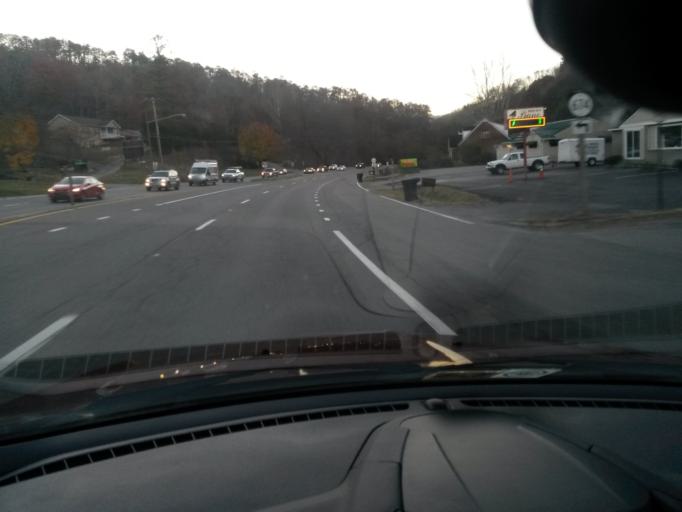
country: US
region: Virginia
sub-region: Roanoke County
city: Narrows
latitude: 37.1993
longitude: -79.9440
